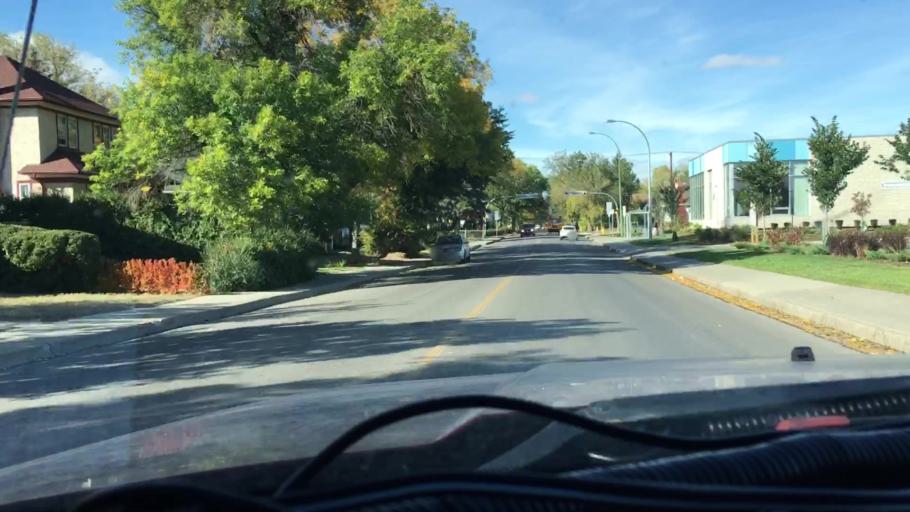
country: CA
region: Saskatchewan
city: Regina
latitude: 50.4587
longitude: -104.6312
